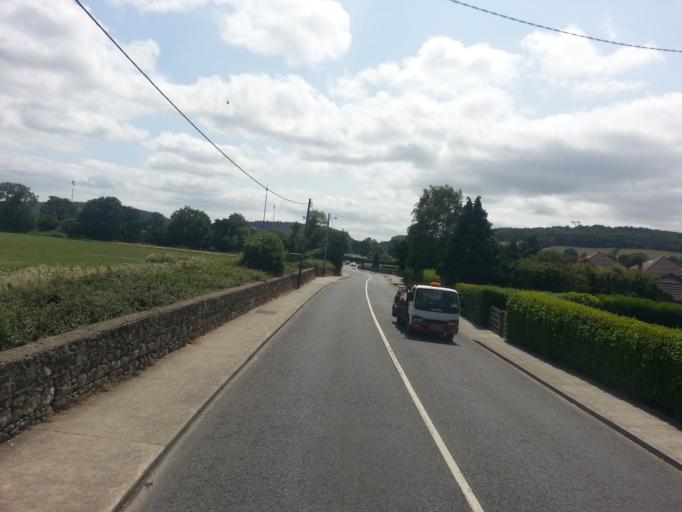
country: IE
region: Leinster
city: Foxrock
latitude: 53.2377
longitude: -6.1954
